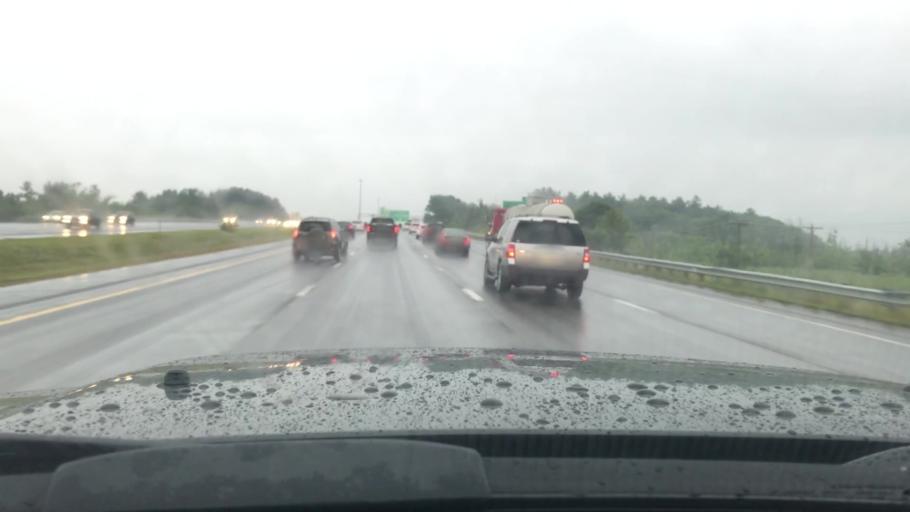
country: US
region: New Hampshire
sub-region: Rockingham County
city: Greenland
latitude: 43.0476
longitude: -70.8133
